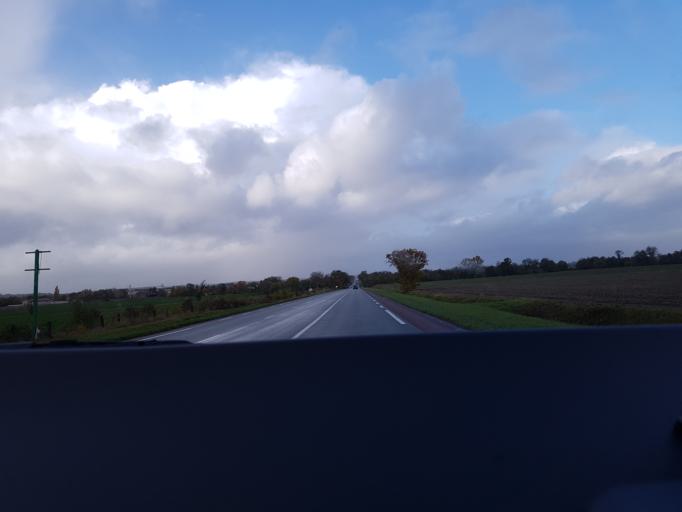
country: FR
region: Poitou-Charentes
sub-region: Departement de la Charente-Maritime
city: Les Gonds
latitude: 45.6887
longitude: -0.6140
